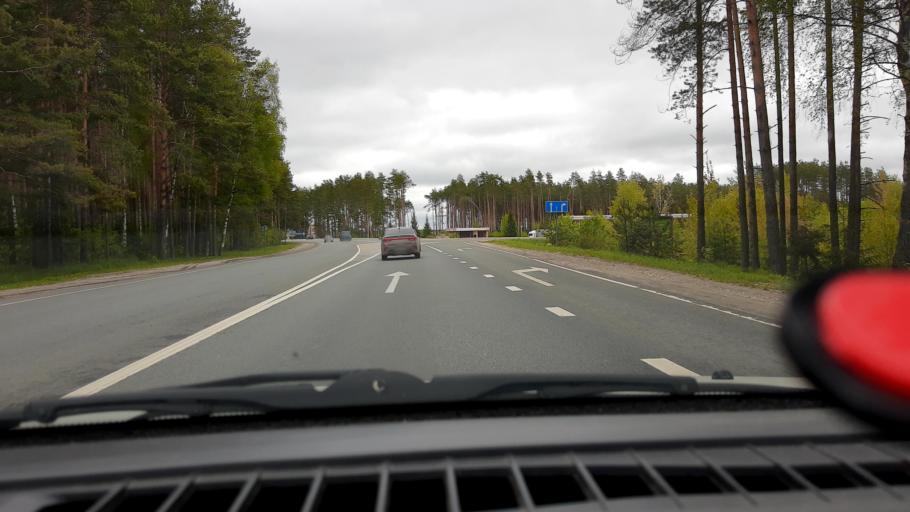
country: RU
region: Nizjnij Novgorod
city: Linda
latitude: 56.6851
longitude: 44.1763
